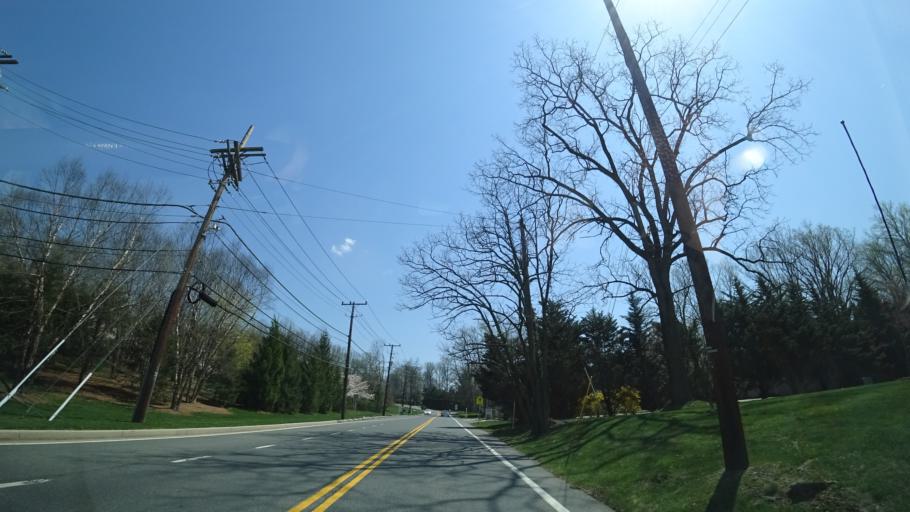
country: US
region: Maryland
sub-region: Montgomery County
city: Cabin John
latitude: 39.0065
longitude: -77.1478
